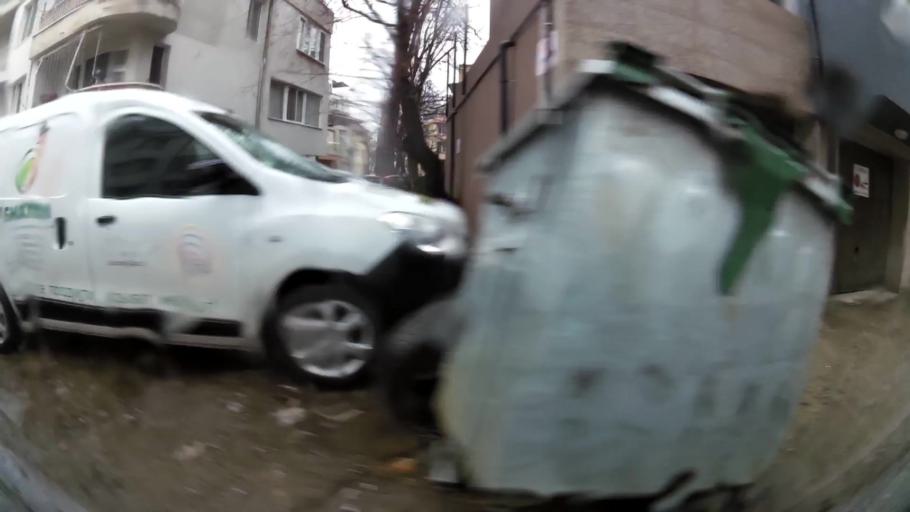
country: BG
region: Sofia-Capital
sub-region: Stolichna Obshtina
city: Sofia
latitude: 42.6493
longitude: 23.3322
